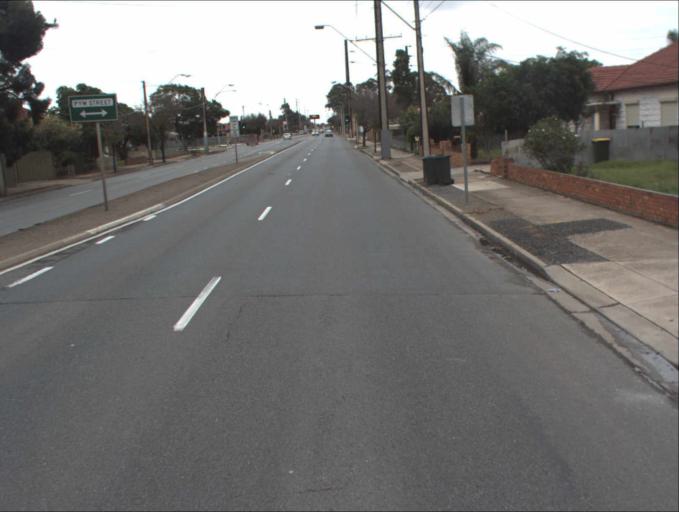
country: AU
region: South Australia
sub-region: Prospect
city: Prospect
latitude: -34.8838
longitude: 138.5719
